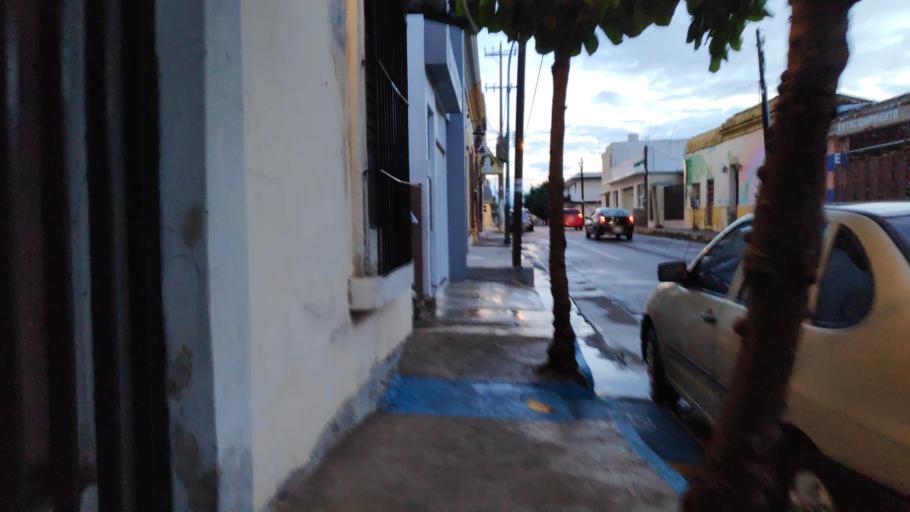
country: MX
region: Sinaloa
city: Culiacan
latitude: 24.8080
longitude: -107.4029
